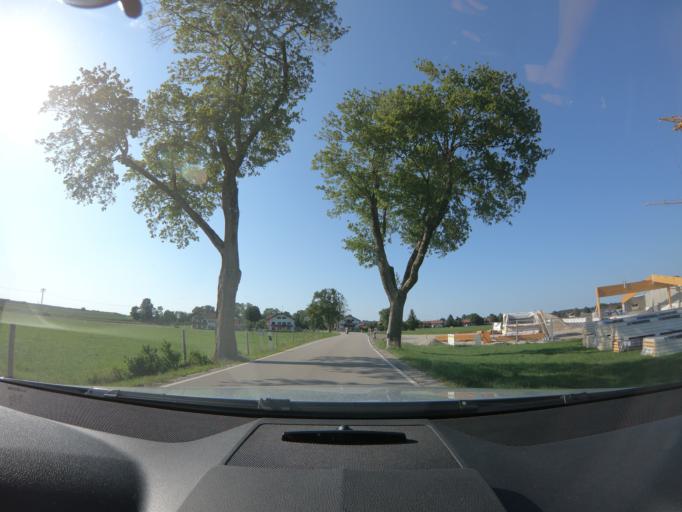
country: DE
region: Bavaria
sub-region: Upper Bavaria
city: Holzkirchen
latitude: 47.8639
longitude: 11.7131
